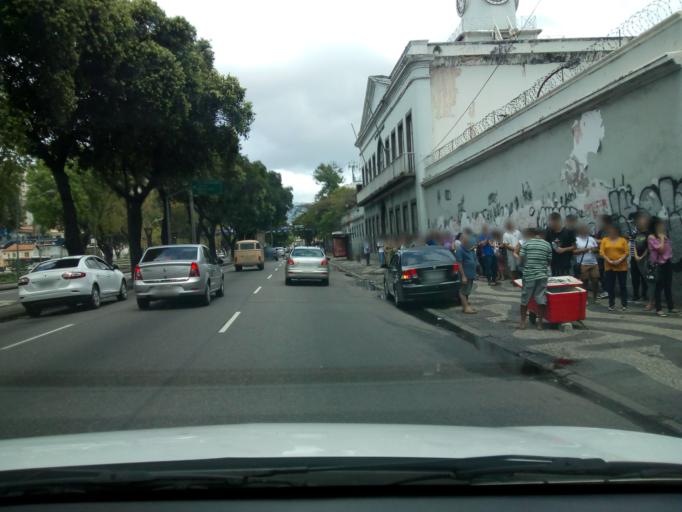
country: BR
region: Rio de Janeiro
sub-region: Rio De Janeiro
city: Rio de Janeiro
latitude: -22.9075
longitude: -43.1996
